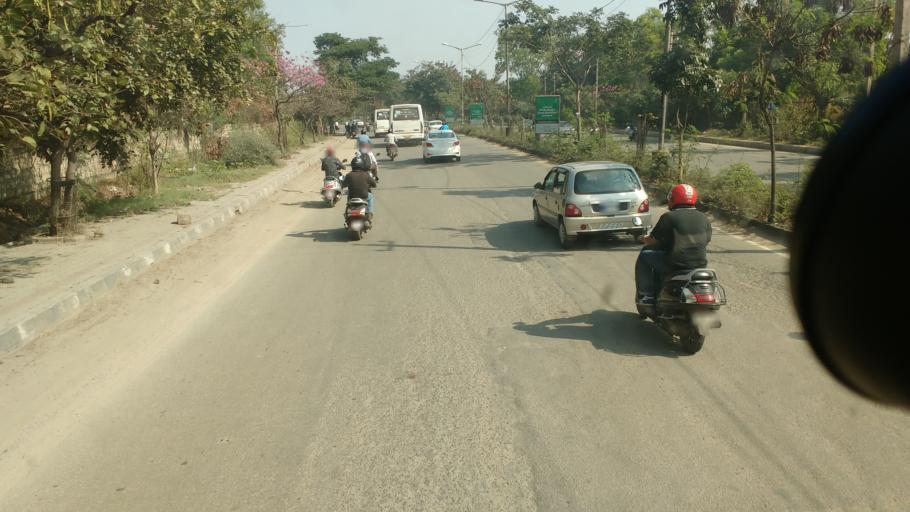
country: IN
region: Karnataka
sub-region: Bangalore Urban
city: Bangalore
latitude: 12.9464
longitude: 77.6402
